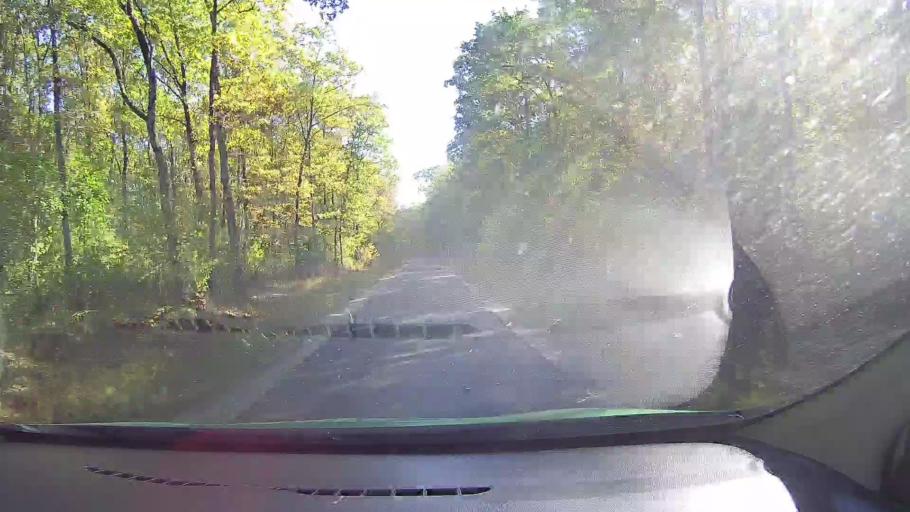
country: RO
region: Satu Mare
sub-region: Comuna Doba
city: Doba
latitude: 47.7091
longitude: 22.7542
